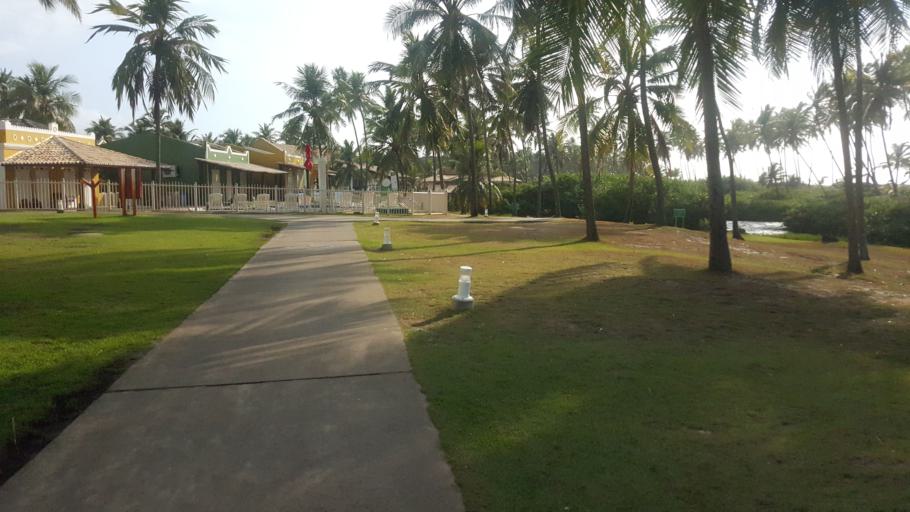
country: BR
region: Bahia
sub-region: Mata De Sao Joao
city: Mata de Sao Joao
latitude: -12.4392
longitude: -37.9207
